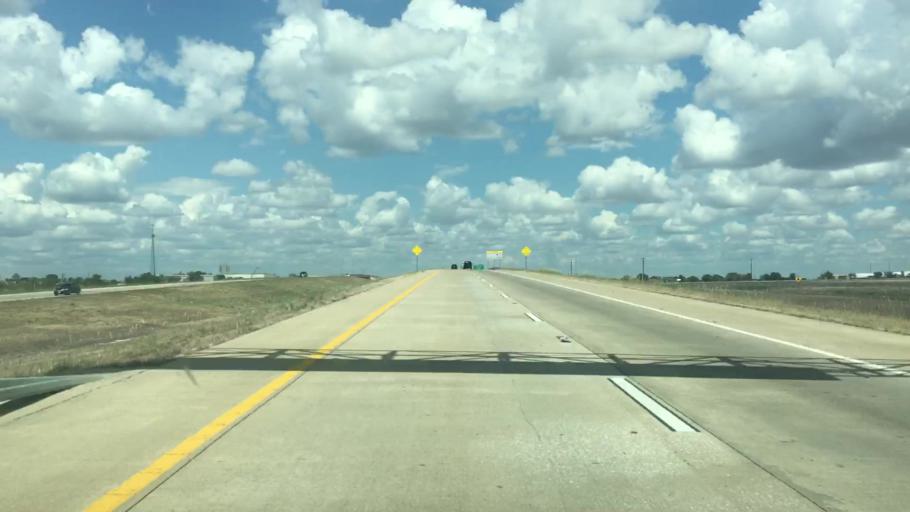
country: US
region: Texas
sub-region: Williamson County
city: Hutto
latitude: 30.5724
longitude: -97.5830
